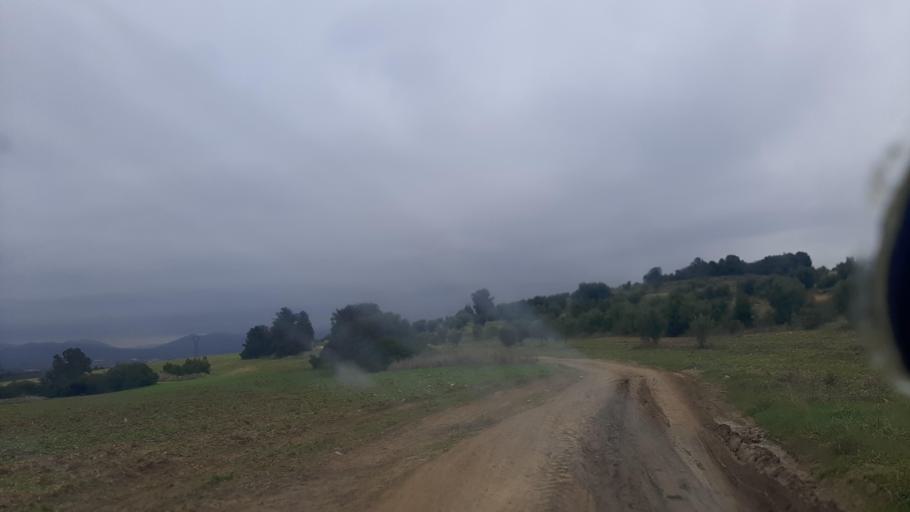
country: TN
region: Tunis
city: La Sebala du Mornag
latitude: 36.5759
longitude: 10.2918
